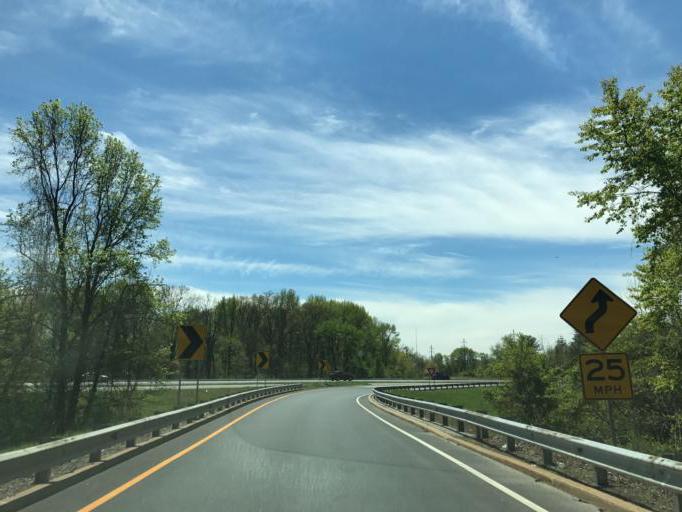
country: US
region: Delaware
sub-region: New Castle County
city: Newport
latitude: 39.7028
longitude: -75.6076
